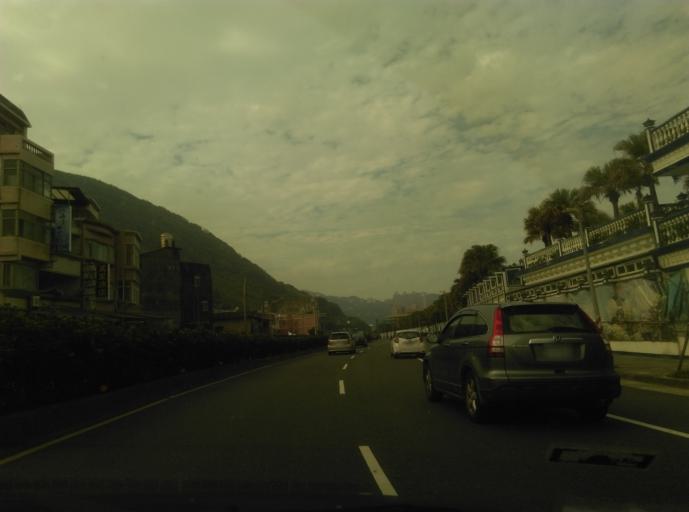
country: TW
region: Taiwan
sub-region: Keelung
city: Keelung
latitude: 25.1803
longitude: 121.6903
